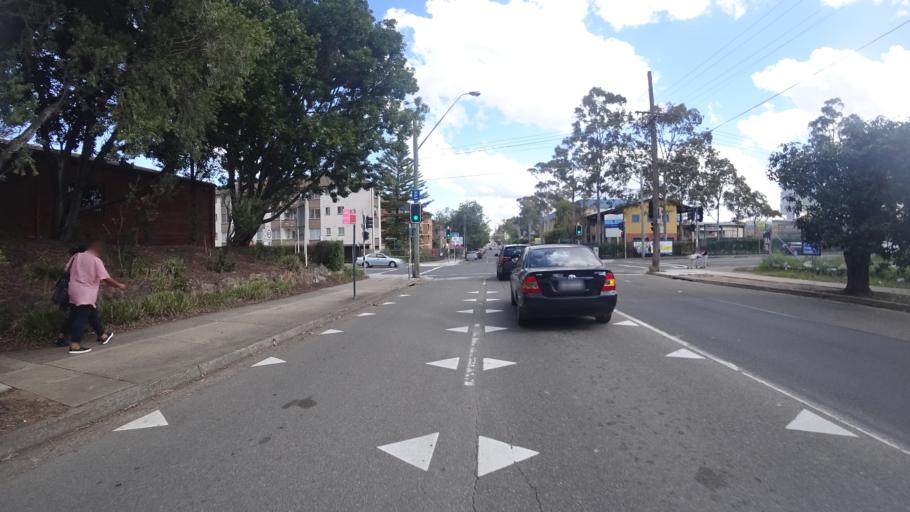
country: AU
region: New South Wales
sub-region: Fairfield
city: Liverpool
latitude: -33.9179
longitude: 150.9279
